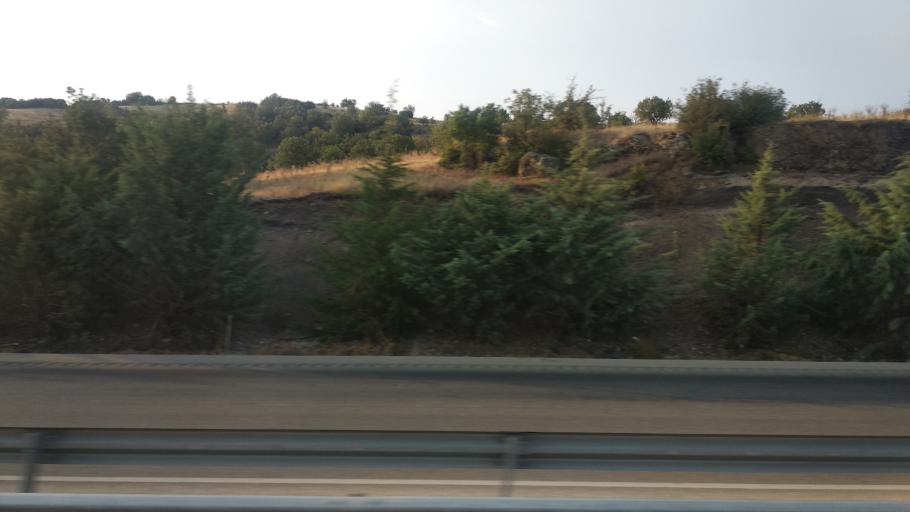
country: TR
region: Manisa
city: Menye
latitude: 38.5658
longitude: 28.5601
